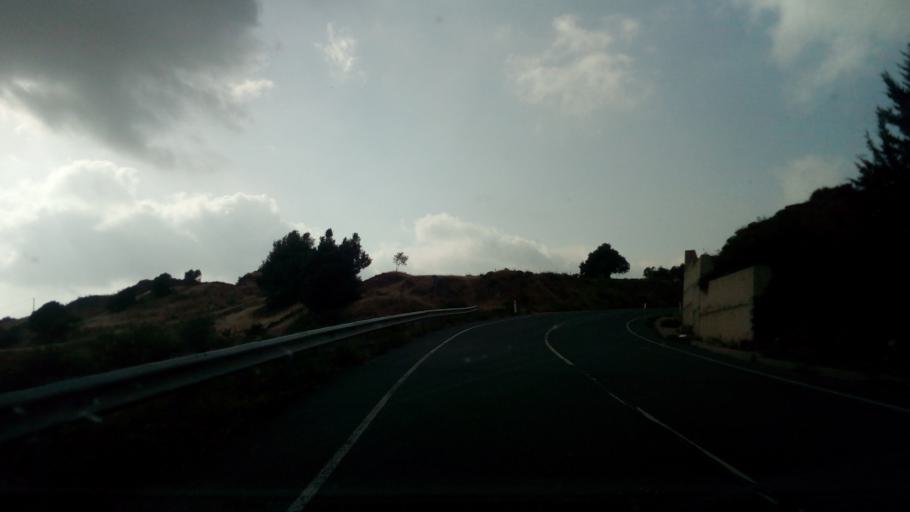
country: CY
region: Limassol
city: Pissouri
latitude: 34.8029
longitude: 32.6485
